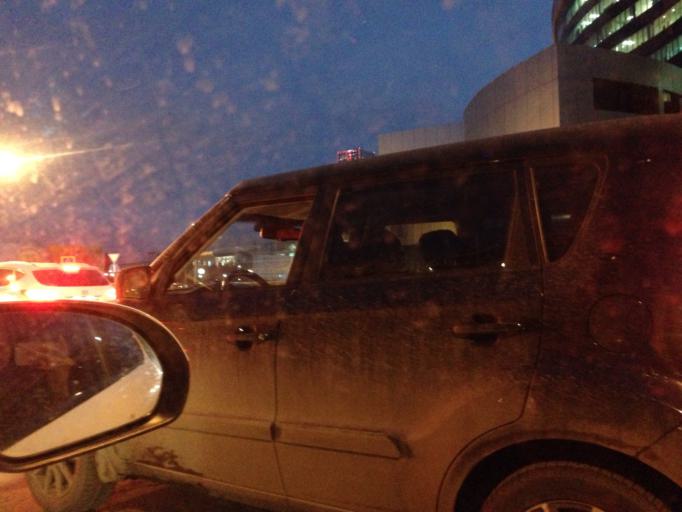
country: KZ
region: Astana Qalasy
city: Astana
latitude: 51.1667
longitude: 71.4129
